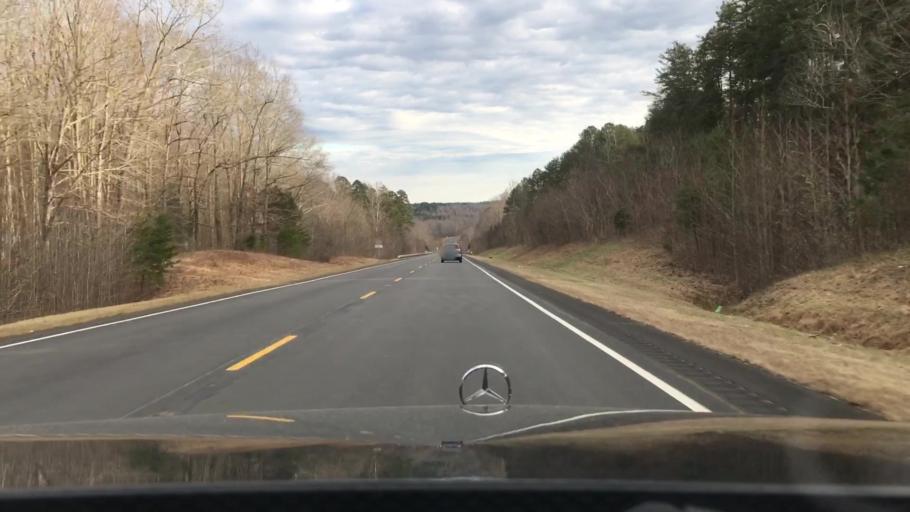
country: US
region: North Carolina
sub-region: Caswell County
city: Yanceyville
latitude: 36.3239
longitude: -79.2342
